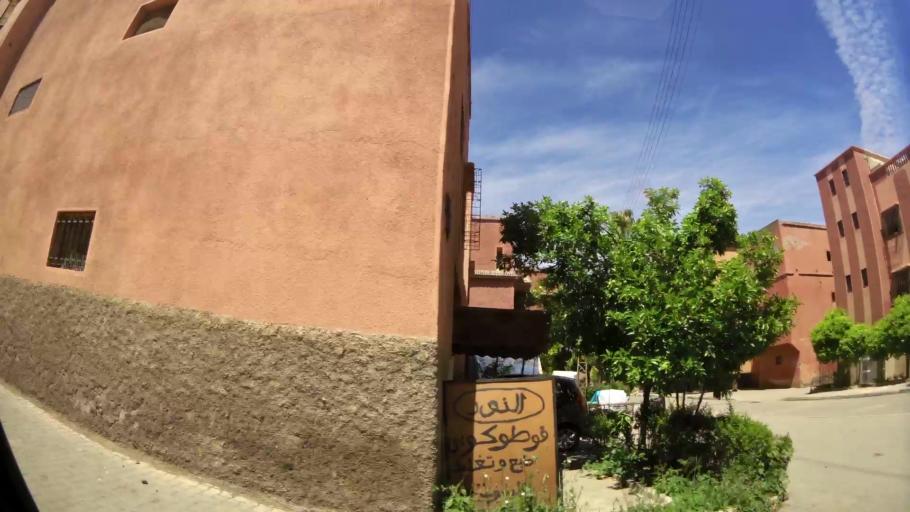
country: MA
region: Marrakech-Tensift-Al Haouz
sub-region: Marrakech
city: Marrakesh
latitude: 31.6574
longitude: -7.9975
